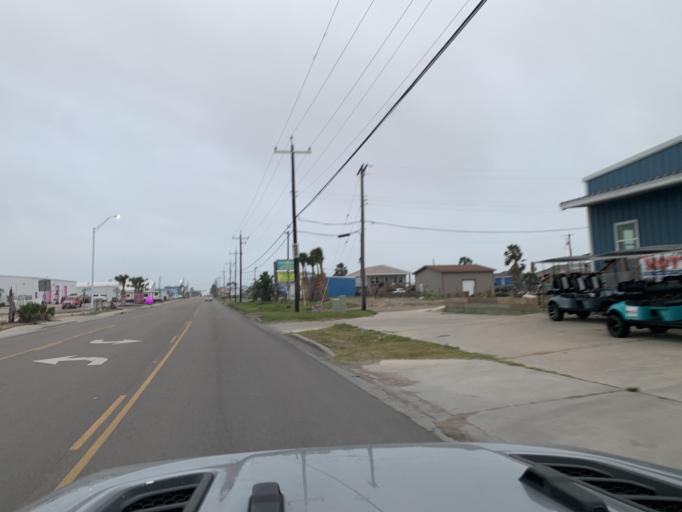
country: US
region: Texas
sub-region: Nueces County
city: Port Aransas
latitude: 27.8309
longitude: -97.0710
